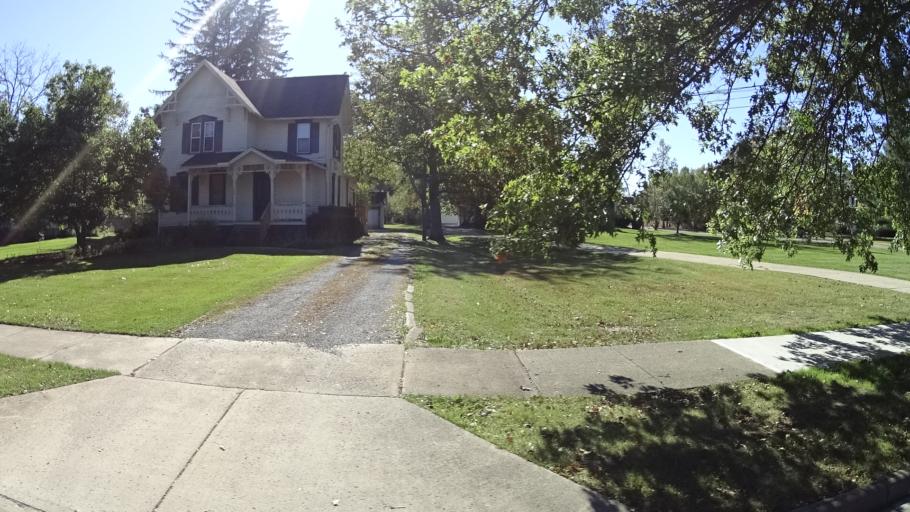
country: US
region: Ohio
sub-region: Lorain County
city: Oberlin
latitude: 41.2914
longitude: -82.2051
